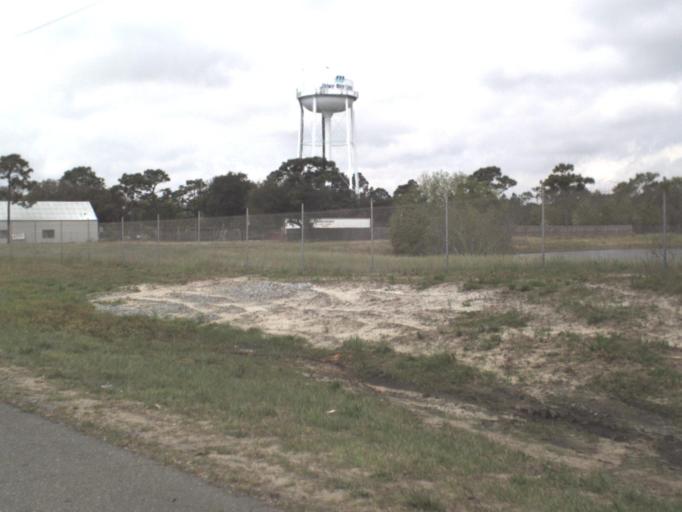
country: US
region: Florida
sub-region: Santa Rosa County
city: Tiger Point
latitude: 30.3903
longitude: -87.0645
